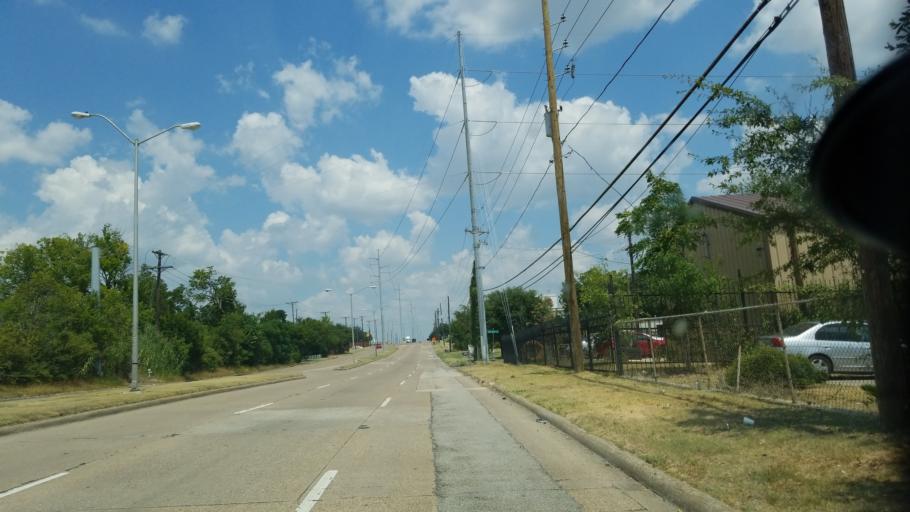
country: US
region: Texas
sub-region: Dallas County
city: Duncanville
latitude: 32.6788
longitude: -96.8913
